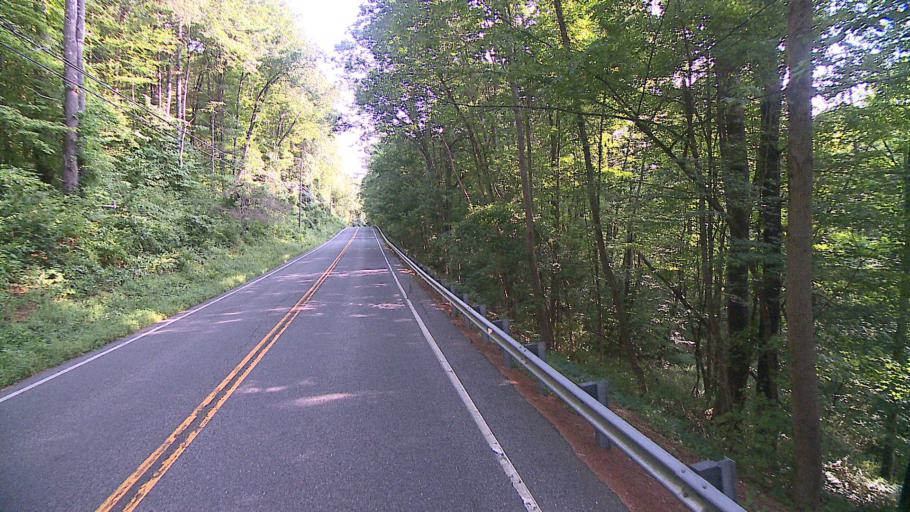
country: US
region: Connecticut
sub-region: Litchfield County
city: Canaan
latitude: 41.8828
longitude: -73.3673
